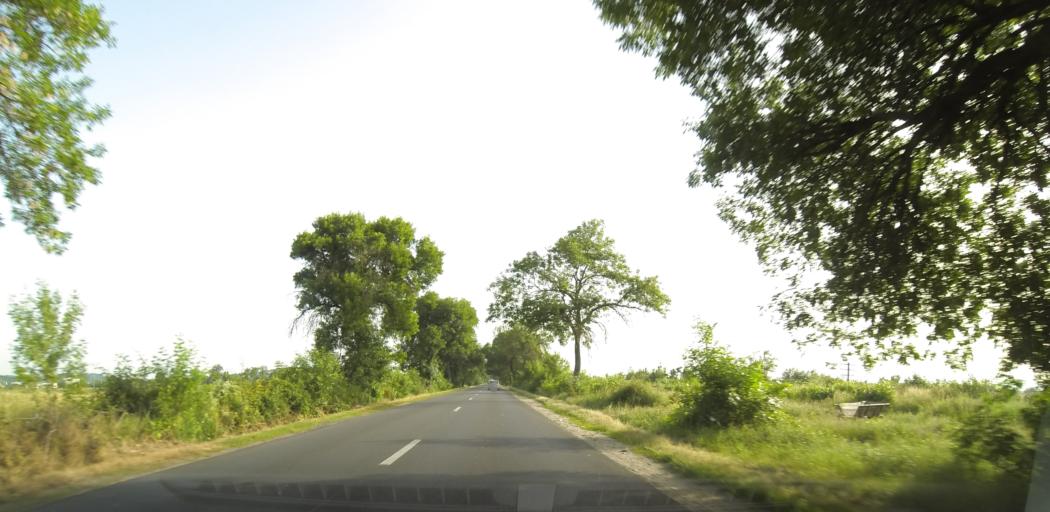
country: RO
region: Valcea
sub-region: Comuna Orlesti
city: Orlesti
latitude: 44.7863
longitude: 24.2449
